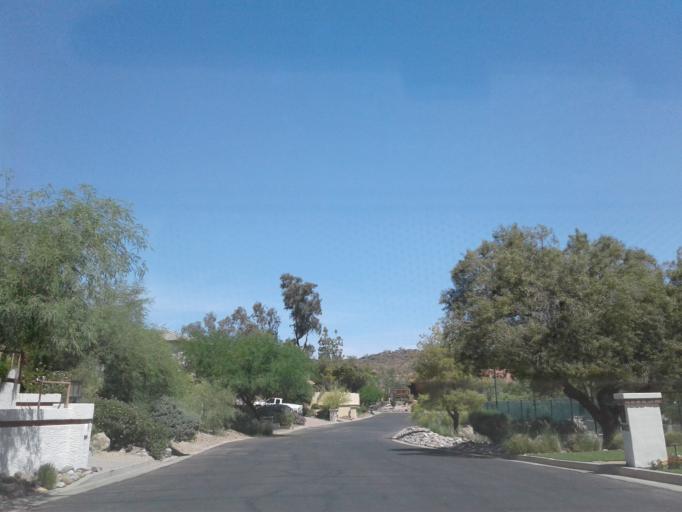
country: US
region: Arizona
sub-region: Maricopa County
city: Paradise Valley
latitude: 33.5771
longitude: -112.0324
